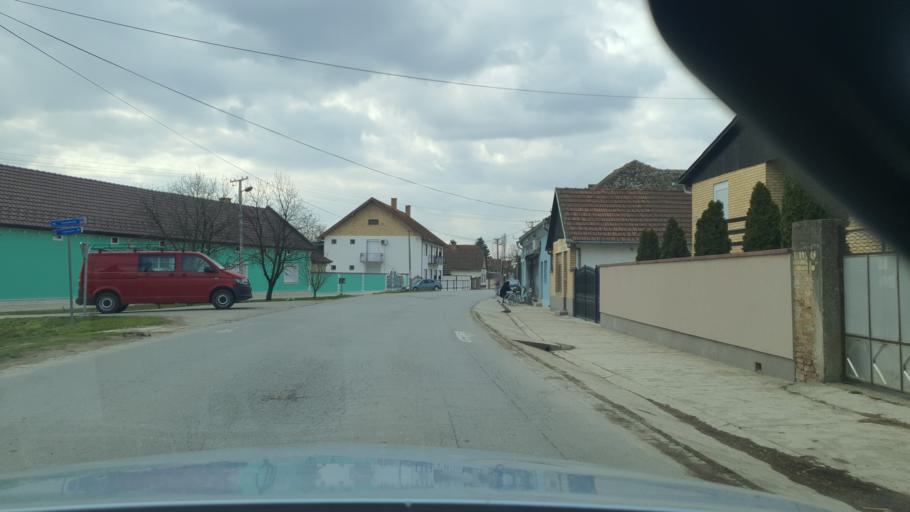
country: RS
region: Autonomna Pokrajina Vojvodina
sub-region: Juznobacki Okrug
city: Bac
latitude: 45.4075
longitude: 19.2943
